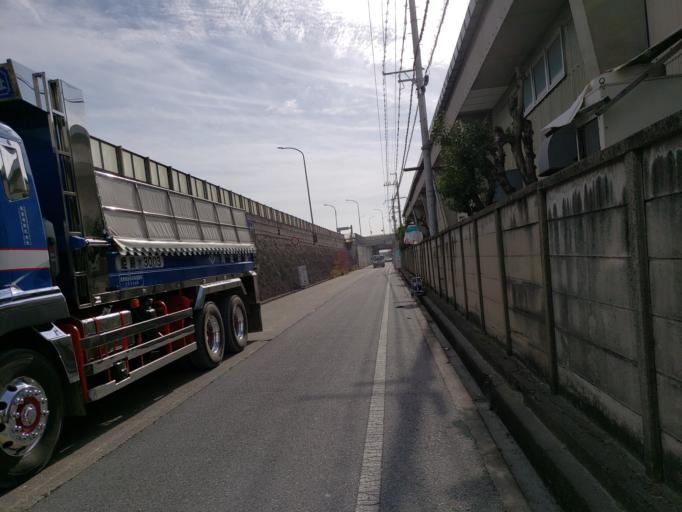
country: JP
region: Hyogo
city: Kakogawacho-honmachi
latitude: 34.7426
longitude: 134.8066
